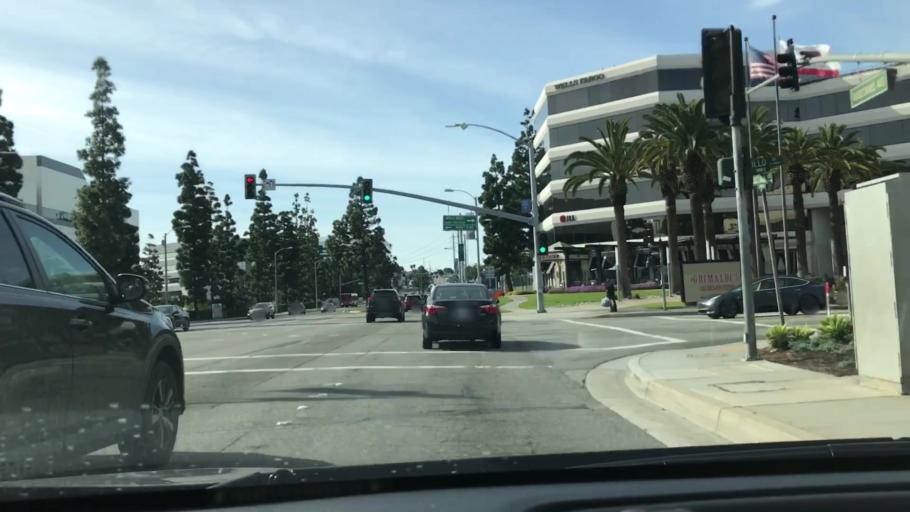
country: US
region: California
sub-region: Los Angeles County
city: Del Aire
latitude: 33.9020
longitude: -118.3862
